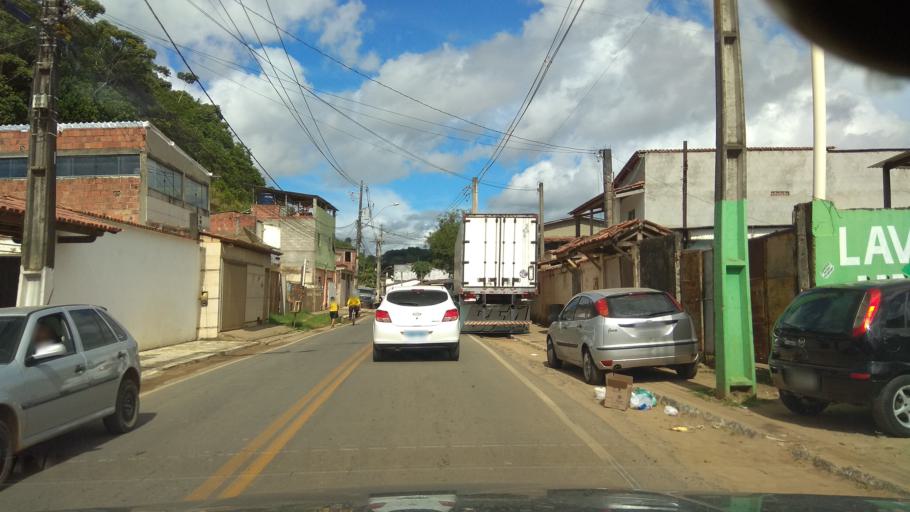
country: BR
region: Bahia
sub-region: Ilheus
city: Ilheus
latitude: -14.7904
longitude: -39.0615
